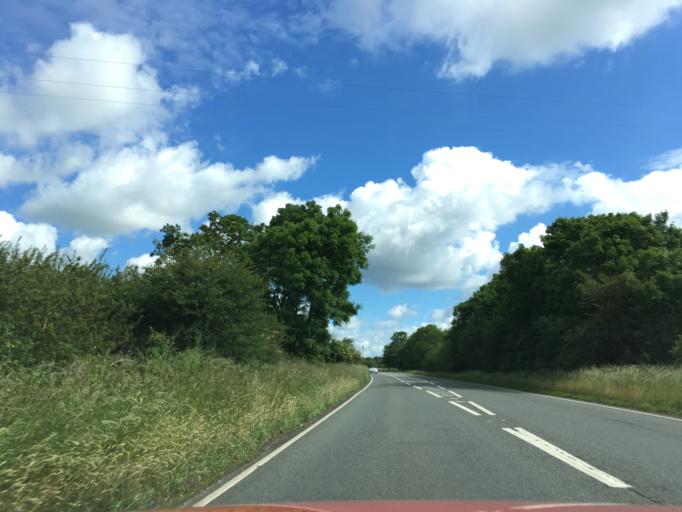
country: GB
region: England
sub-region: Oxfordshire
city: Carterton
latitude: 51.7475
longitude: -1.6532
